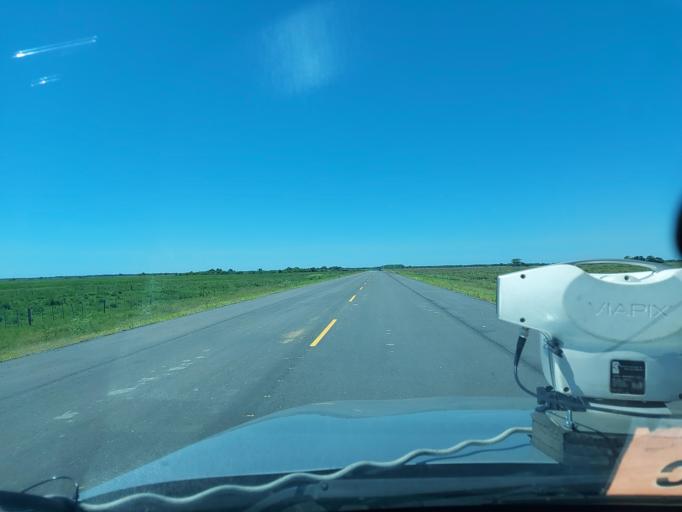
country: PY
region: Neembucu
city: Pilar
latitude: -26.8404
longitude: -58.2296
